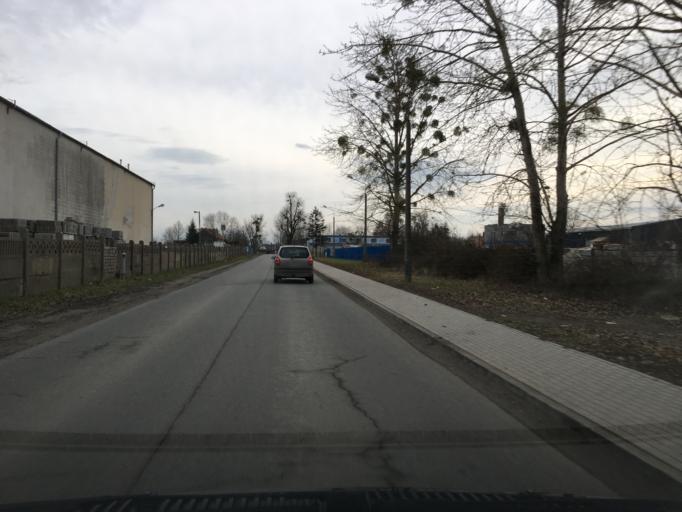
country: PL
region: Opole Voivodeship
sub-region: Powiat kedzierzynsko-kozielski
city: Kozle
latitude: 50.3513
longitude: 18.1410
